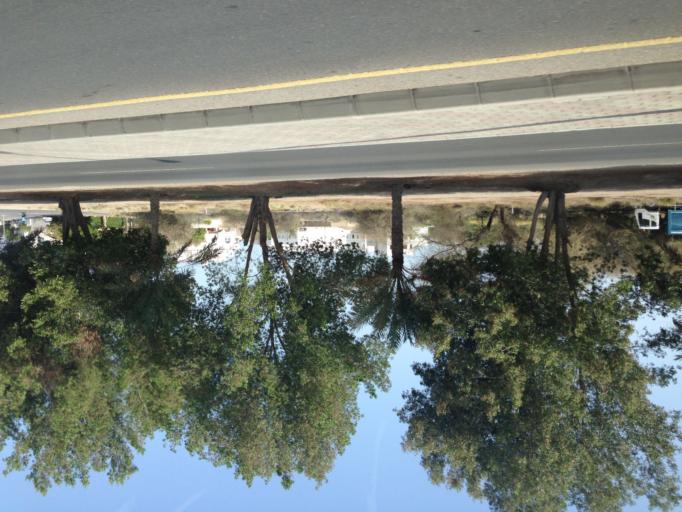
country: OM
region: Muhafazat Masqat
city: As Sib al Jadidah
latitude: 23.6131
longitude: 58.2333
